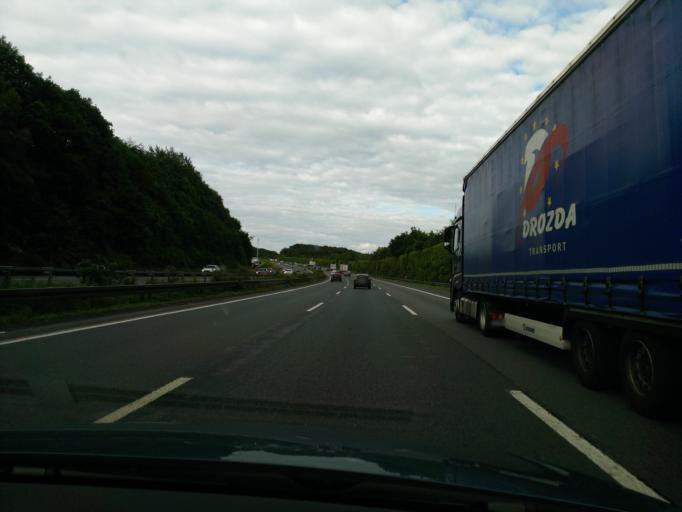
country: DE
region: North Rhine-Westphalia
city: Gevelsberg
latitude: 51.3252
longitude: 7.3044
